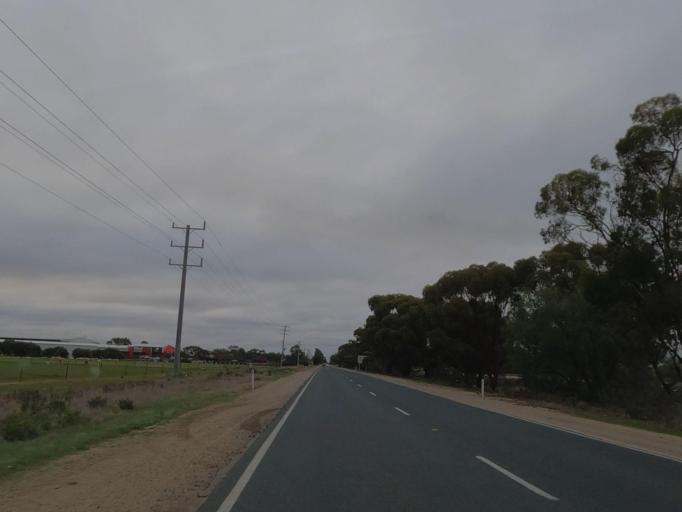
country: AU
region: Victoria
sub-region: Swan Hill
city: Swan Hill
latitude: -35.3901
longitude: 143.5696
